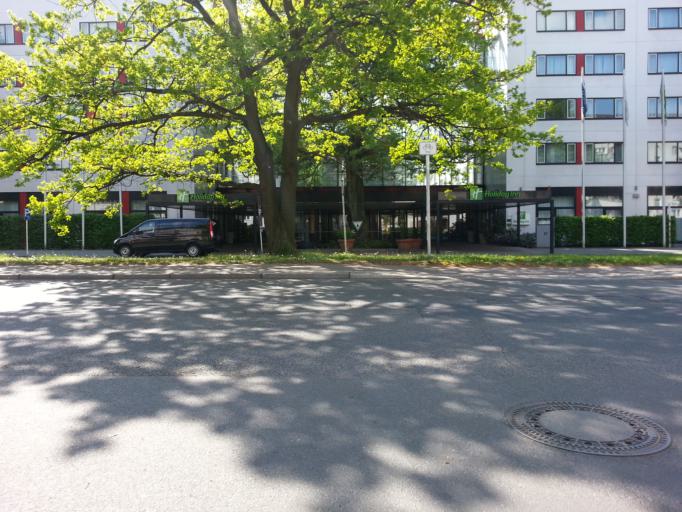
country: DE
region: Berlin
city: Siemensstadt
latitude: 52.5406
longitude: 13.2630
